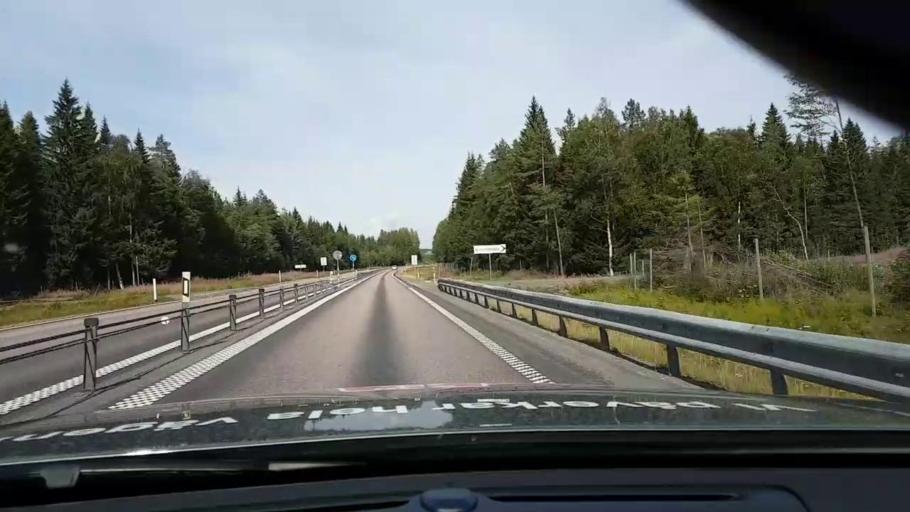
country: SE
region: Vaesternorrland
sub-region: OErnskoeldsviks Kommun
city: Husum
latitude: 63.4357
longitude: 19.2111
